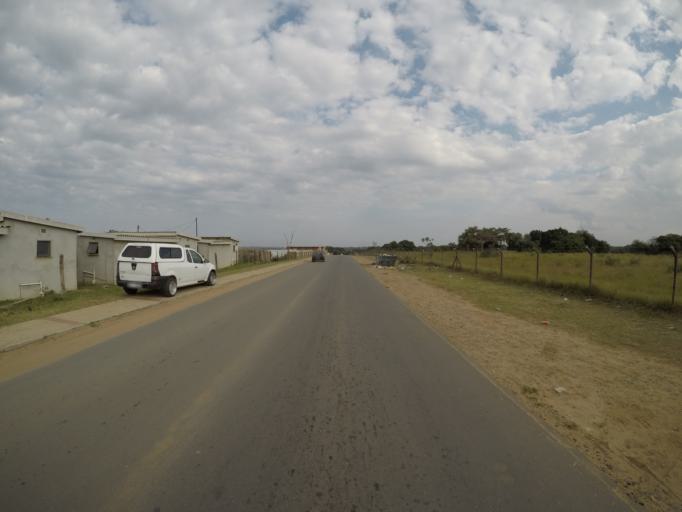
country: ZA
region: KwaZulu-Natal
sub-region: uThungulu District Municipality
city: Richards Bay
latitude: -28.7456
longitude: 32.0899
